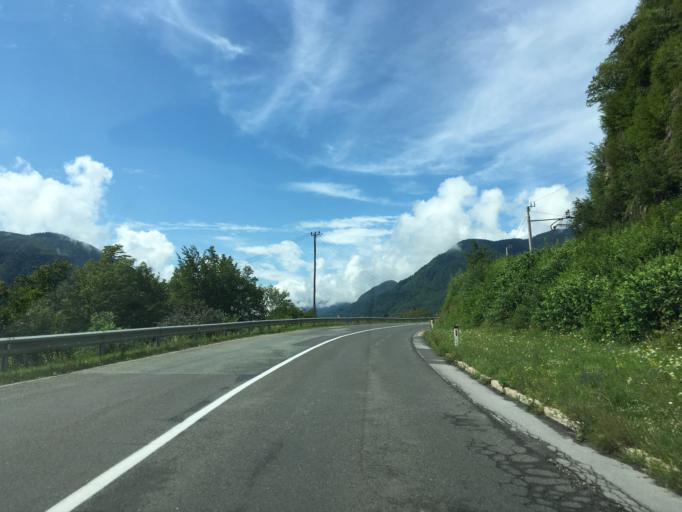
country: SI
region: Bled
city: Zasip
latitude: 46.4169
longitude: 14.1103
